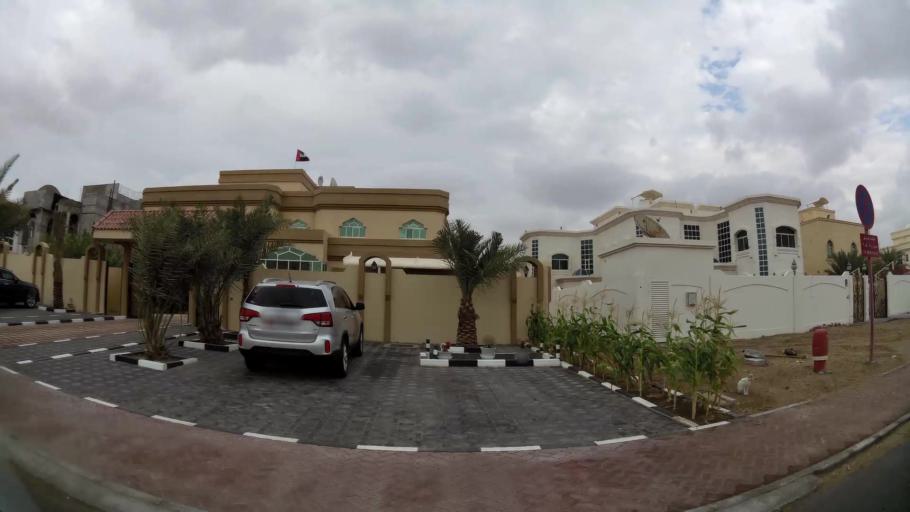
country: AE
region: Abu Dhabi
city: Abu Dhabi
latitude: 24.3540
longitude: 54.6291
